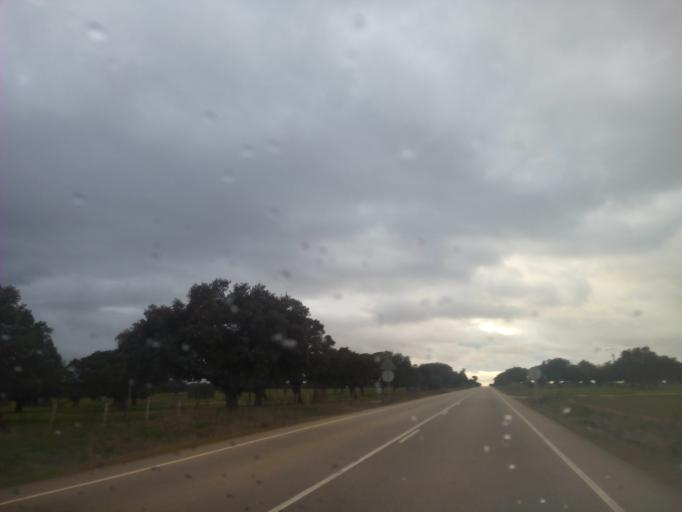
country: ES
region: Castille and Leon
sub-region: Provincia de Salamanca
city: Cabrillas
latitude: 40.7562
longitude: -6.1904
